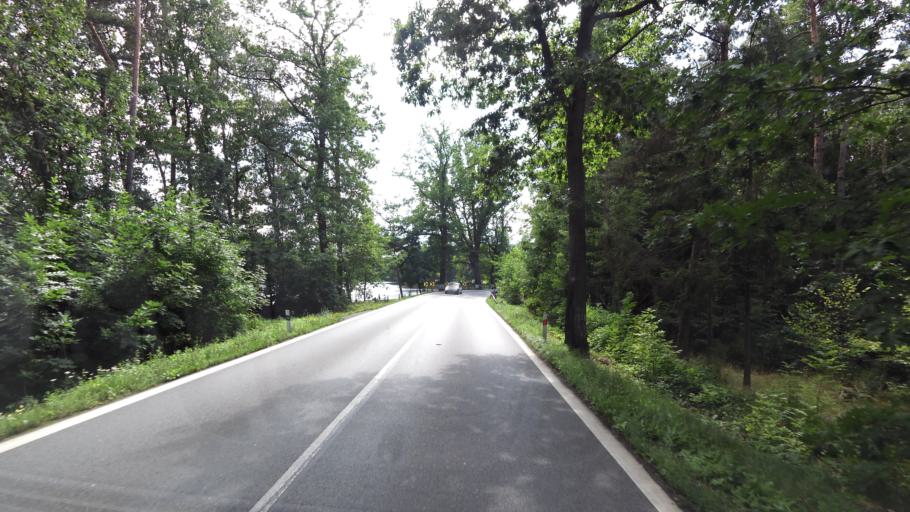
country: CZ
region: Plzensky
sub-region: Okres Domazlice
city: Klenci pod Cerchovem
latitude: 49.4113
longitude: 12.8668
